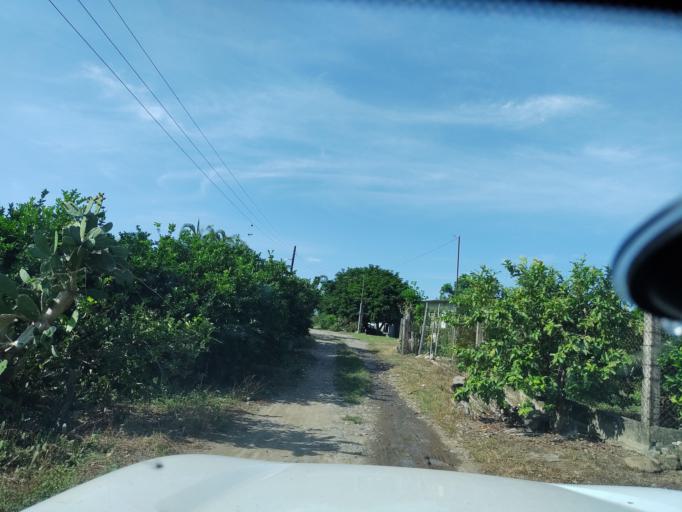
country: MX
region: Veracruz
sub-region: Misantla
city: La Defensa
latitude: 20.1108
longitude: -96.9869
